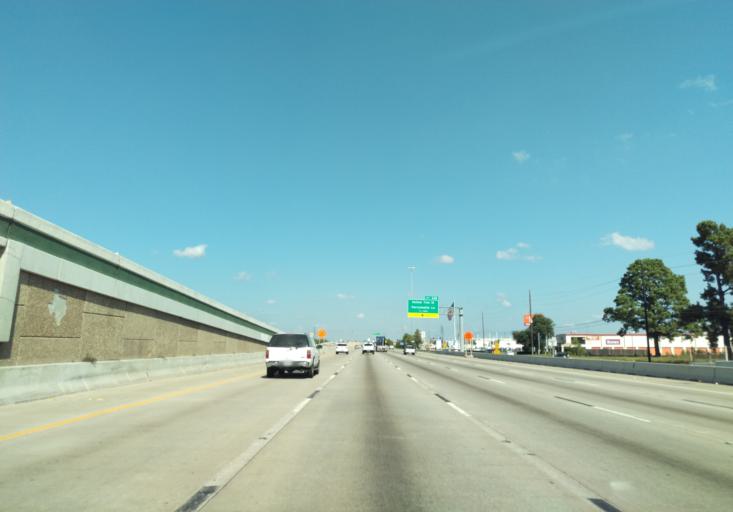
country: US
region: Texas
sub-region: Harris County
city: Spring
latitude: 30.0140
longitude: -95.4281
